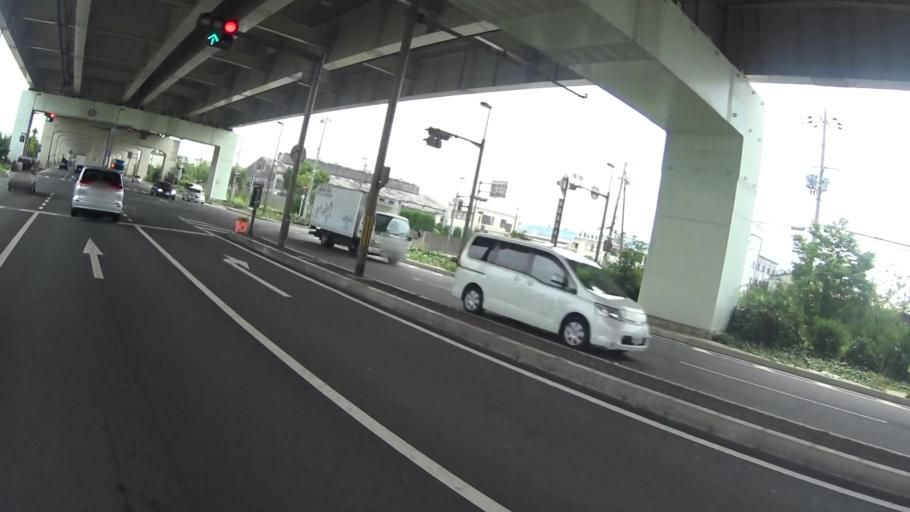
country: JP
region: Kyoto
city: Yawata
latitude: 34.8851
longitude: 135.7491
